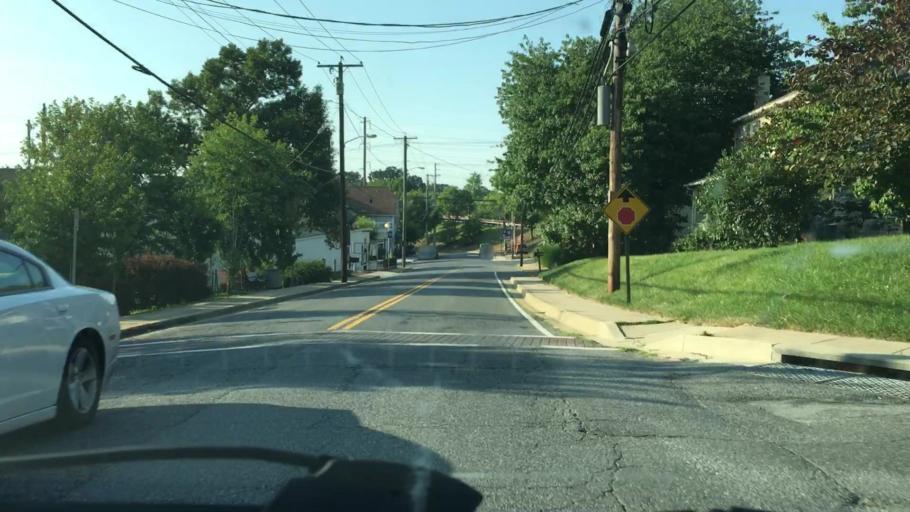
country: US
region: Maryland
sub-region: Prince George's County
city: Glenn Dale
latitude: 39.0058
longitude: -76.7786
